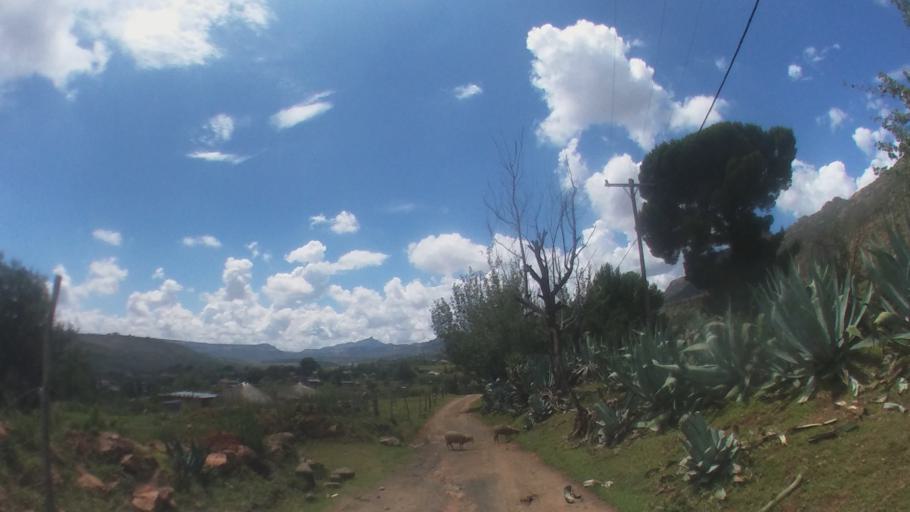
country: LS
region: Maseru
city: Nako
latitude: -29.6243
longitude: 27.5141
